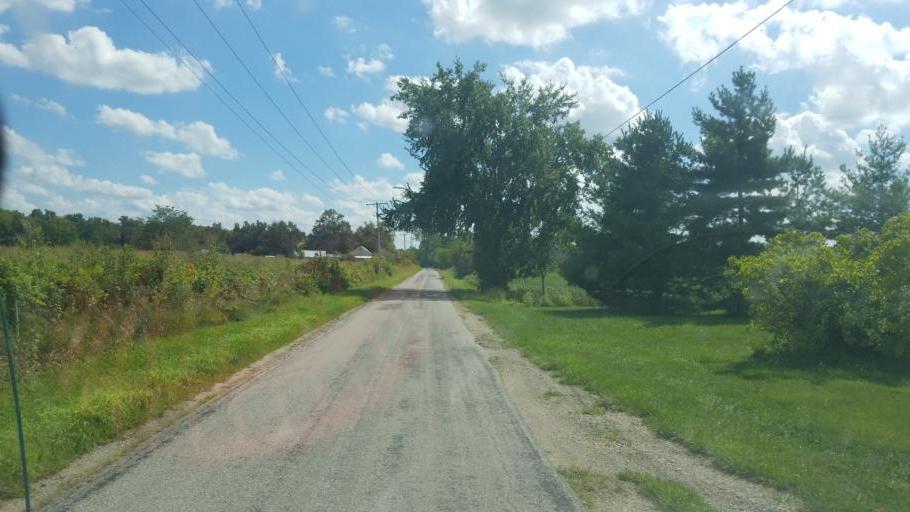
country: US
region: Ohio
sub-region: Union County
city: Richwood
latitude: 40.3450
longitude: -83.2437
